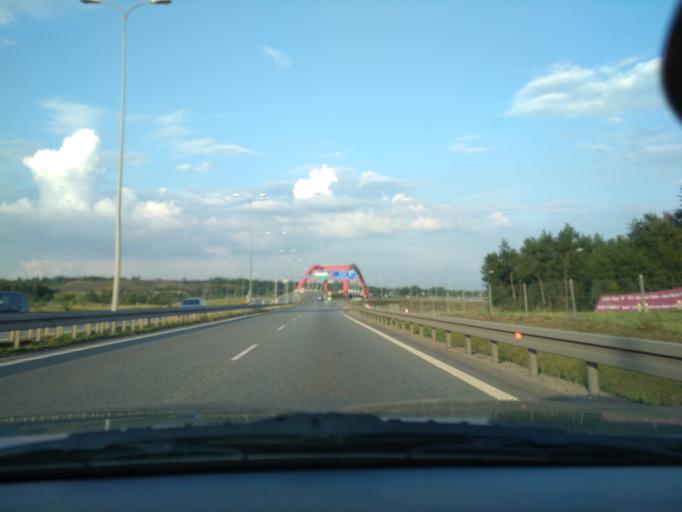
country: PL
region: Silesian Voivodeship
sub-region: Powiat gliwicki
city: Przyszowice
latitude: 50.2686
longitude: 18.7228
